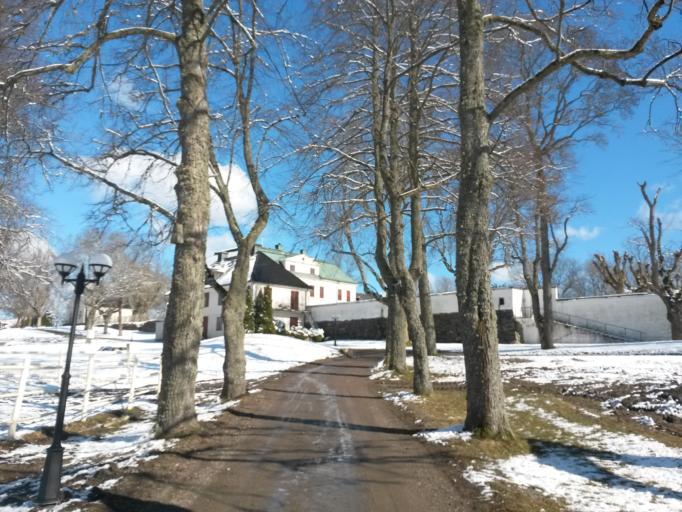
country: SE
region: Stockholm
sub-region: Nynashamns Kommun
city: Osmo
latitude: 59.0386
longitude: 18.0130
